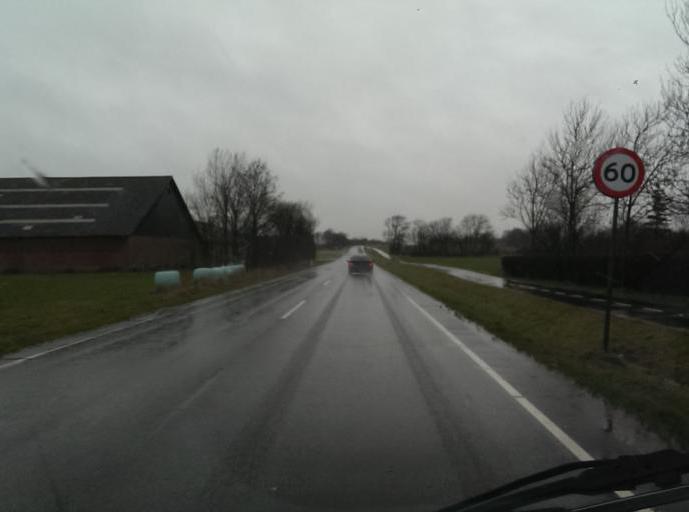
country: DK
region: South Denmark
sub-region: Varde Kommune
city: Olgod
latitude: 55.7215
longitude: 8.6120
